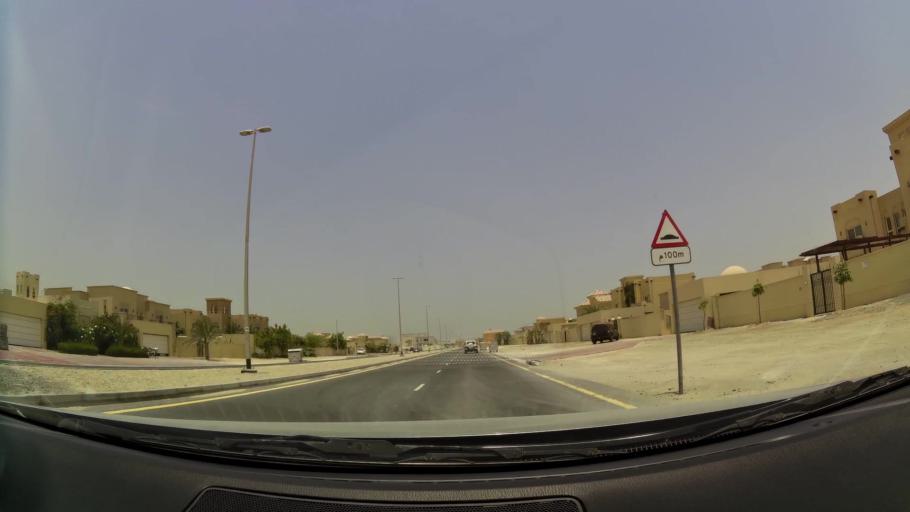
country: AE
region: Dubai
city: Dubai
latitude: 25.0876
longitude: 55.2370
